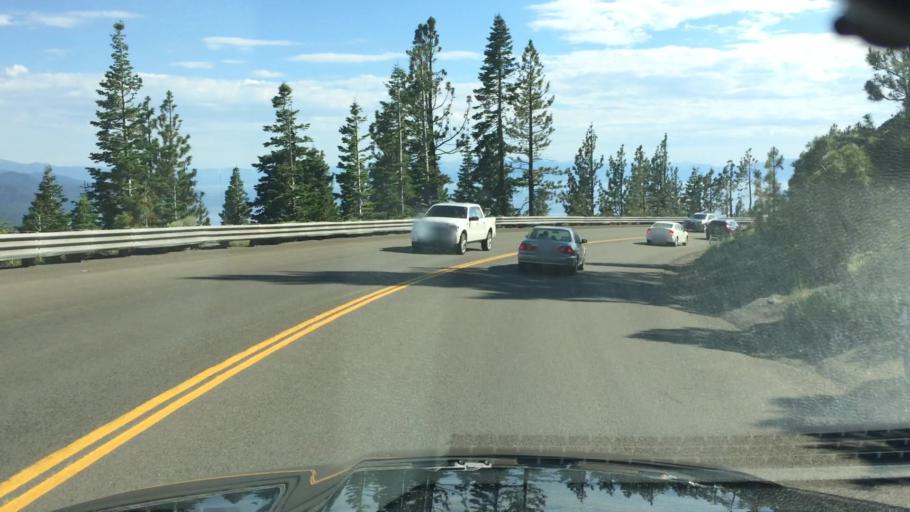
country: US
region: Nevada
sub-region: Washoe County
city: Incline Village
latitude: 39.2633
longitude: -119.9293
